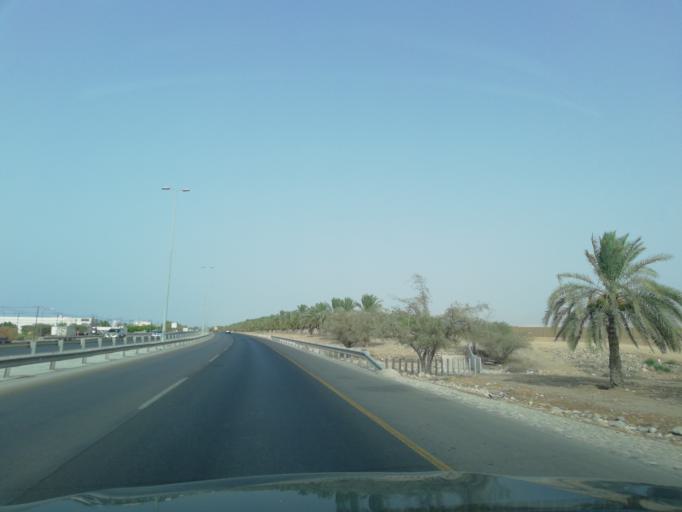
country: OM
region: Muhafazat Masqat
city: As Sib al Jadidah
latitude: 23.5890
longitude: 58.2255
